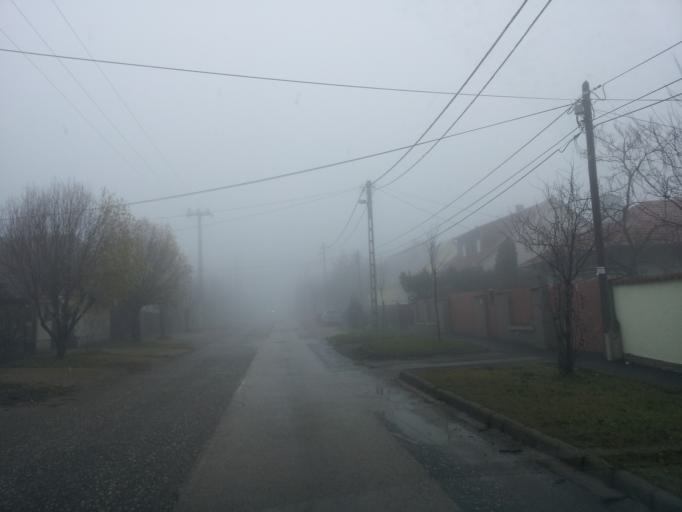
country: HU
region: Pest
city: Toeroekbalint
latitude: 47.4194
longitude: 18.8884
